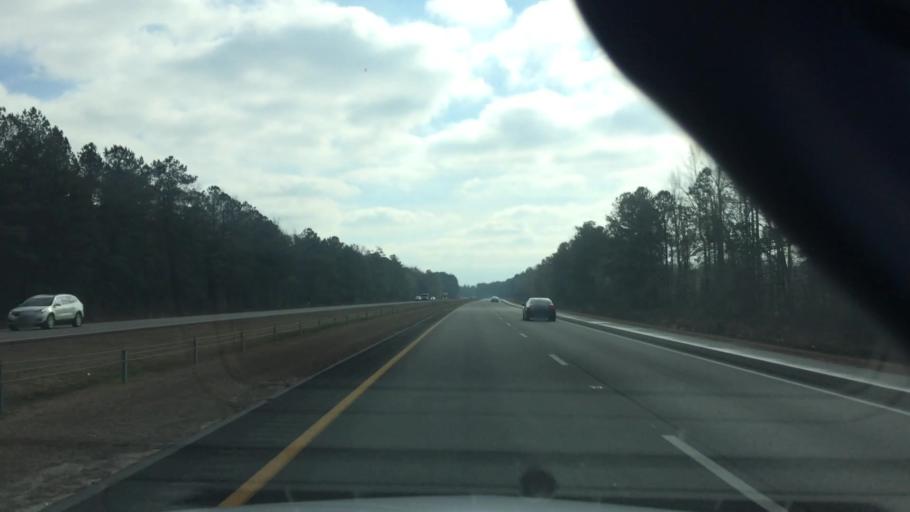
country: US
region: North Carolina
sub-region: Pender County
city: Burgaw
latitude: 34.5464
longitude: -77.8935
